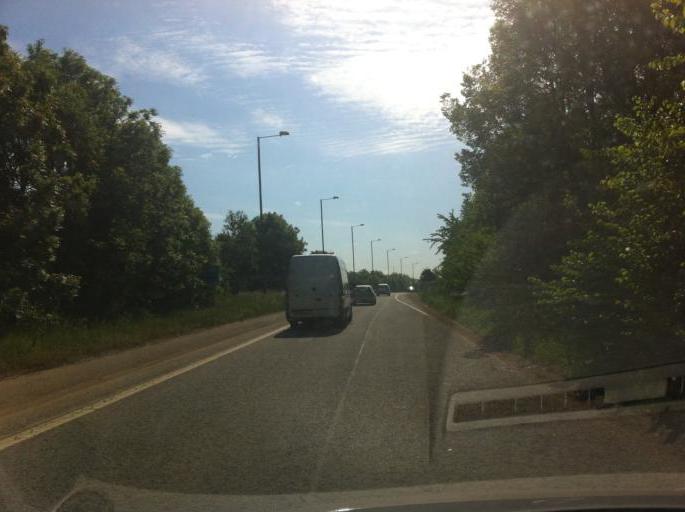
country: GB
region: England
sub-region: Greater London
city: Hayes
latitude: 51.4924
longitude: -0.4087
